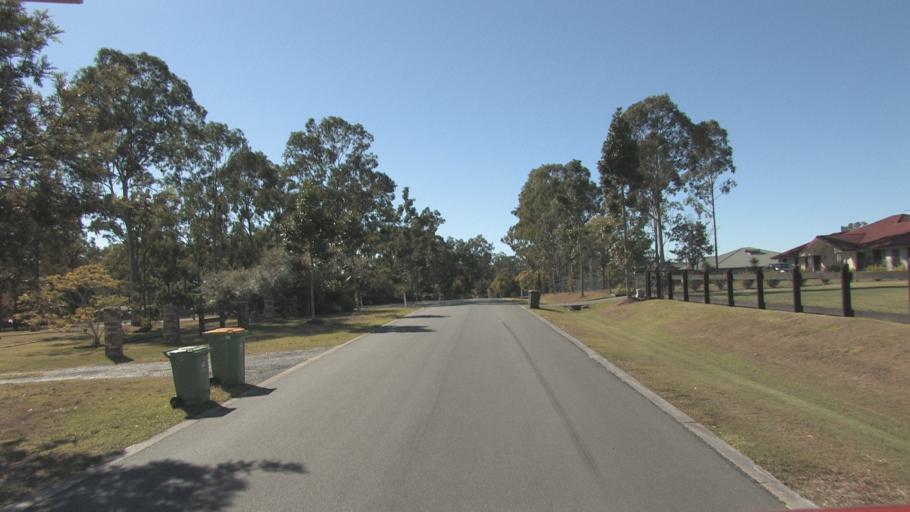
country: AU
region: Queensland
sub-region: Logan
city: North Maclean
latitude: -27.7467
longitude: 152.9487
